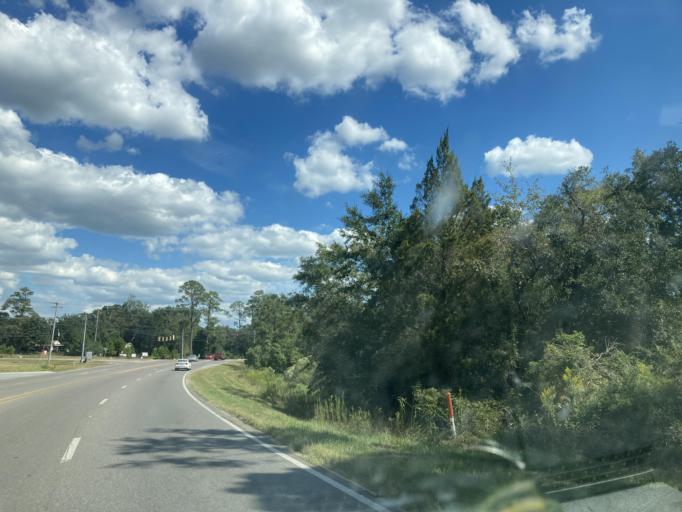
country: US
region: Mississippi
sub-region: Jackson County
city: Gulf Hills
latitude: 30.4442
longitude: -88.8410
